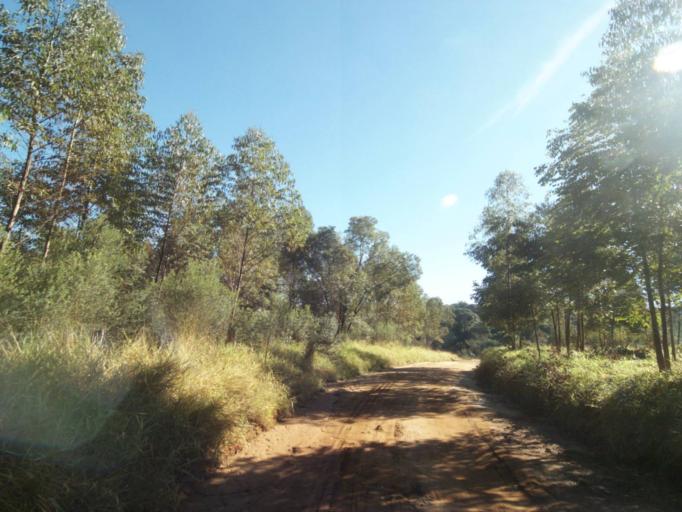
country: BR
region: Parana
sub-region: Tibagi
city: Tibagi
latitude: -24.5383
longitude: -50.3689
